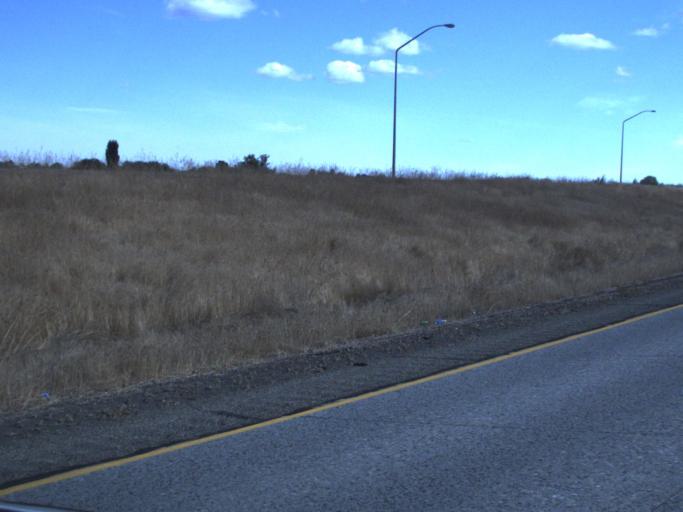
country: US
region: Washington
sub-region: Yakima County
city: Grandview
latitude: 46.2716
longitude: -119.9274
